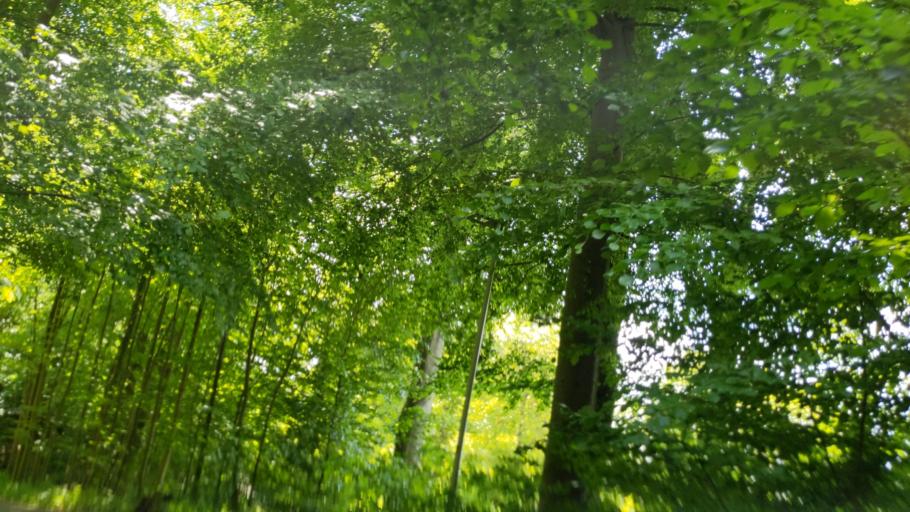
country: DE
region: Schleswig-Holstein
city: Ratzeburg
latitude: 53.7019
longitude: 10.7867
